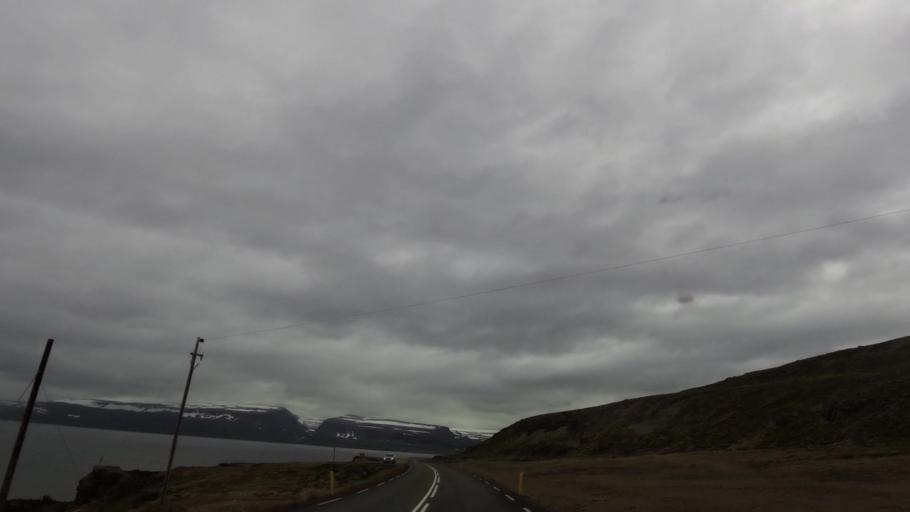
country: IS
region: Westfjords
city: Isafjoerdur
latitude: 66.0497
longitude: -22.7679
